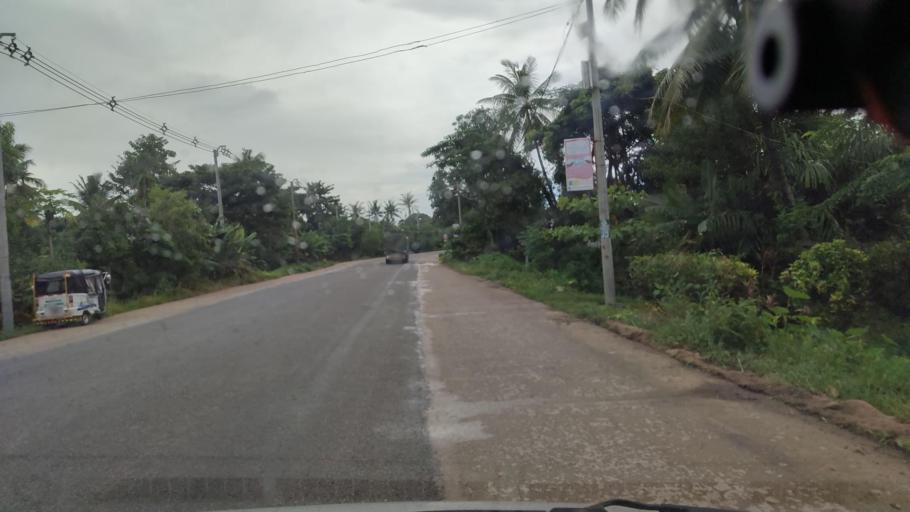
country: MM
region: Bago
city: Tharyarwady
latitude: 17.3558
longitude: 95.9060
